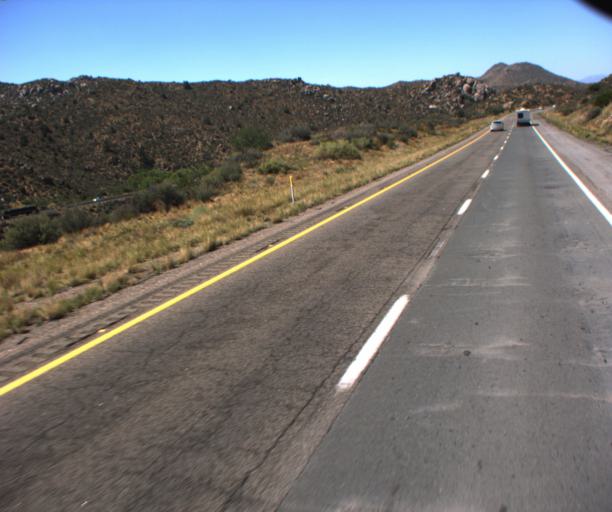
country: US
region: Arizona
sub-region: Mohave County
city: Peach Springs
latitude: 35.1765
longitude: -113.4990
